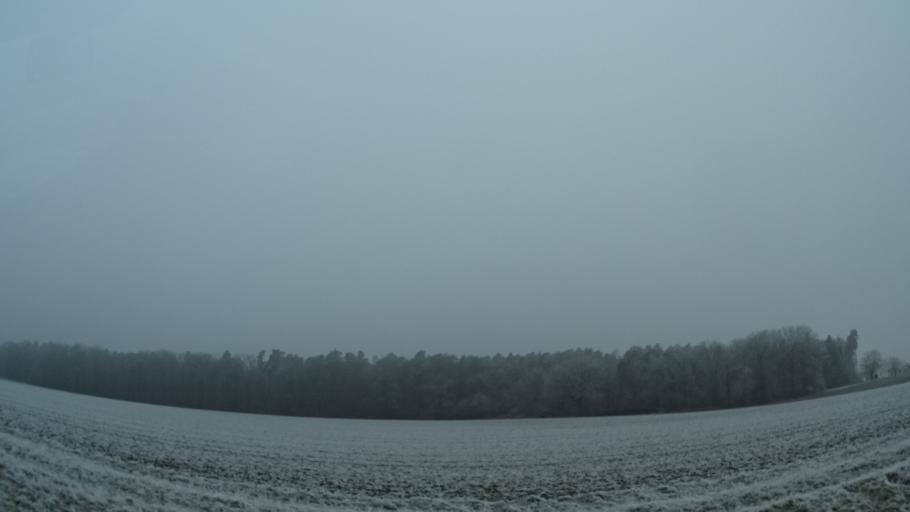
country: DE
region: Bavaria
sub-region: Regierungsbezirk Unterfranken
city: Frankenwinheim
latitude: 49.8585
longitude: 10.2951
